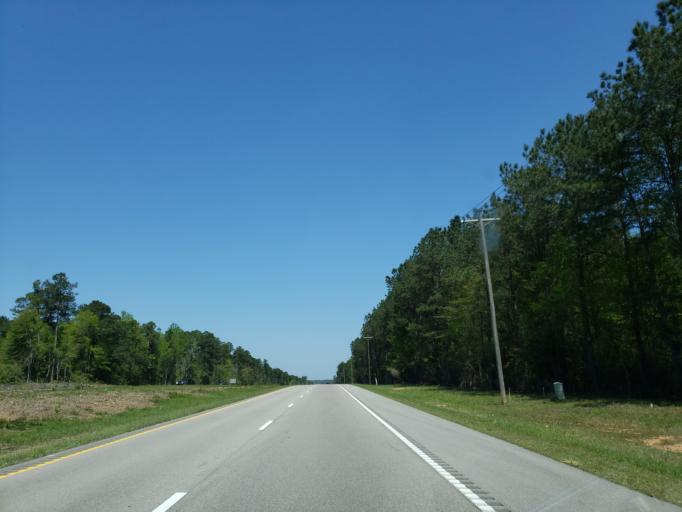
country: US
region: Mississippi
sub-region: Stone County
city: Wiggins
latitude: 31.0237
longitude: -89.2018
